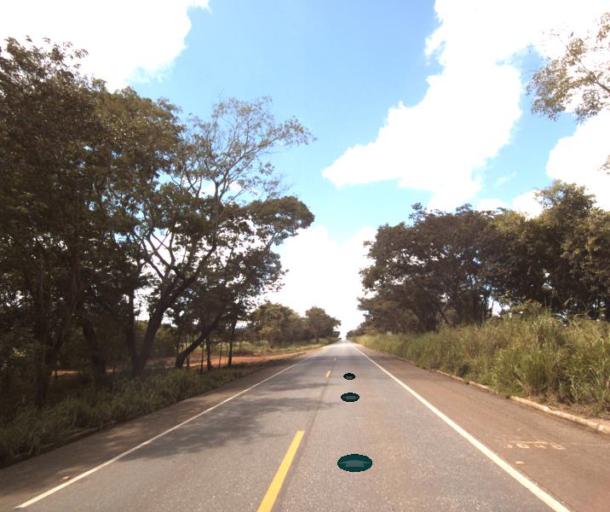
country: BR
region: Goias
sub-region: Petrolina De Goias
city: Petrolina de Goias
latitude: -15.9413
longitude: -49.1959
